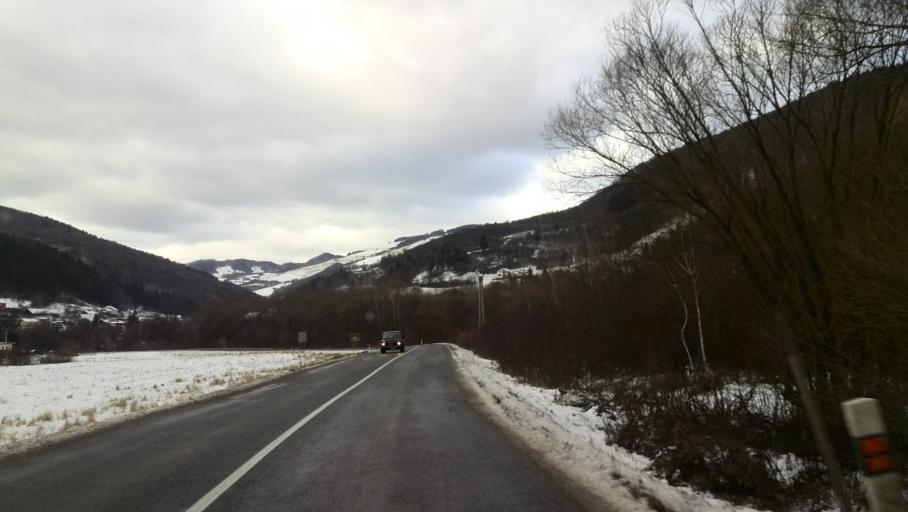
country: SK
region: Kosicky
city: Gelnica
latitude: 48.8678
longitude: 20.9695
